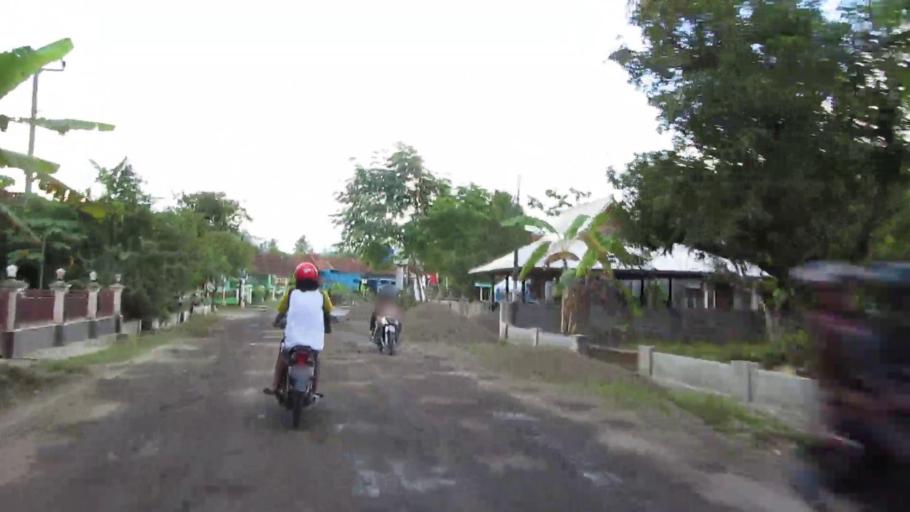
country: ID
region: West Java
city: Binangun
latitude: -7.7183
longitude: 108.4749
